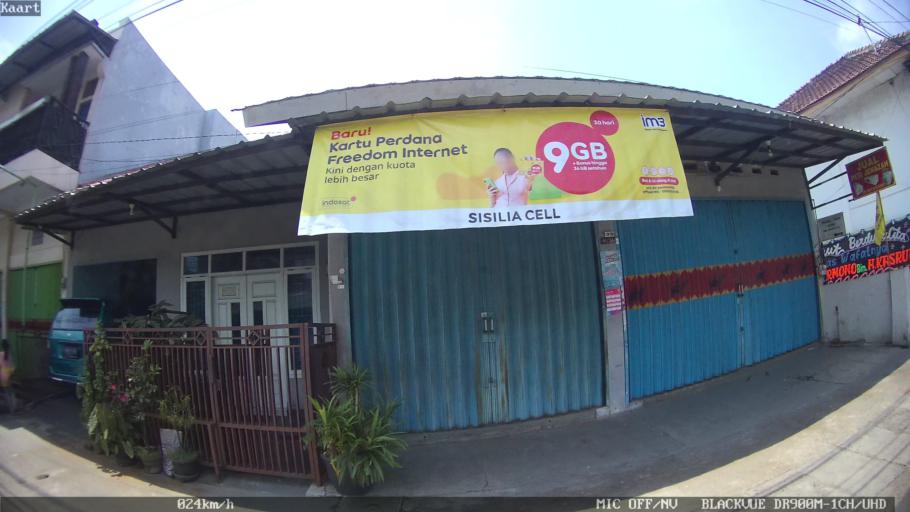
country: ID
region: Lampung
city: Kedaton
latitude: -5.4005
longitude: 105.2564
